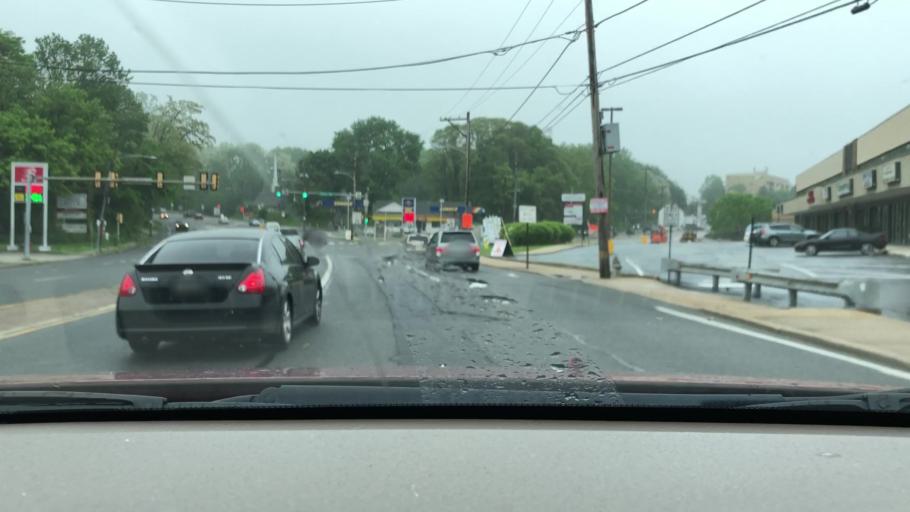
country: US
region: Pennsylvania
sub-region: Delaware County
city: Springfield
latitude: 39.9454
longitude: -75.3265
